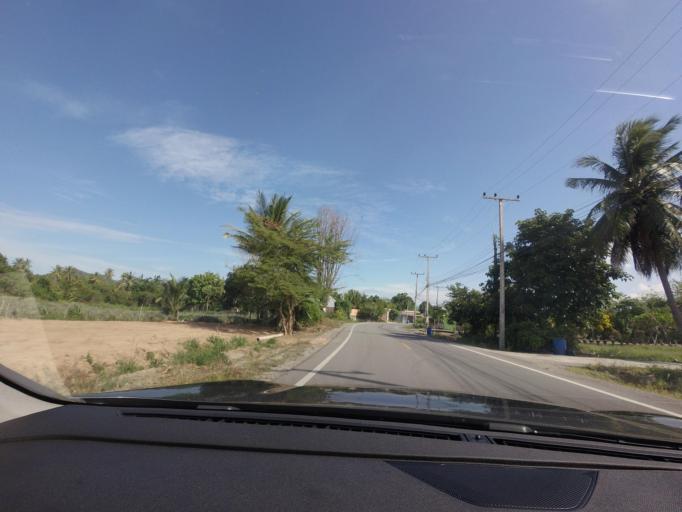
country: TH
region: Prachuap Khiri Khan
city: Pran Buri
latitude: 12.4440
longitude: 99.9450
